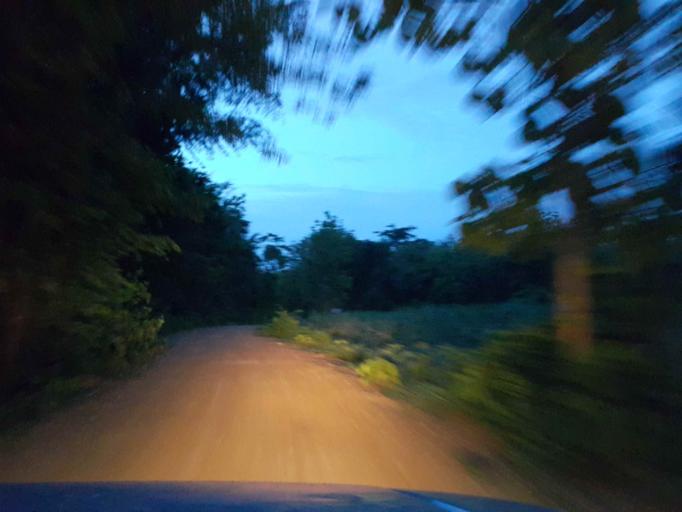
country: TH
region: Sukhothai
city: Thung Saliam
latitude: 17.2220
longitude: 99.5467
